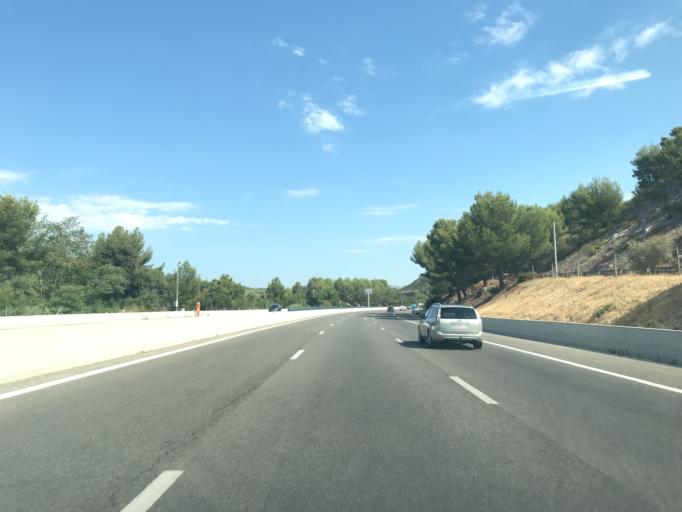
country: FR
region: Provence-Alpes-Cote d'Azur
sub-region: Departement du Var
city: Bandol
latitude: 43.1540
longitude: 5.7653
